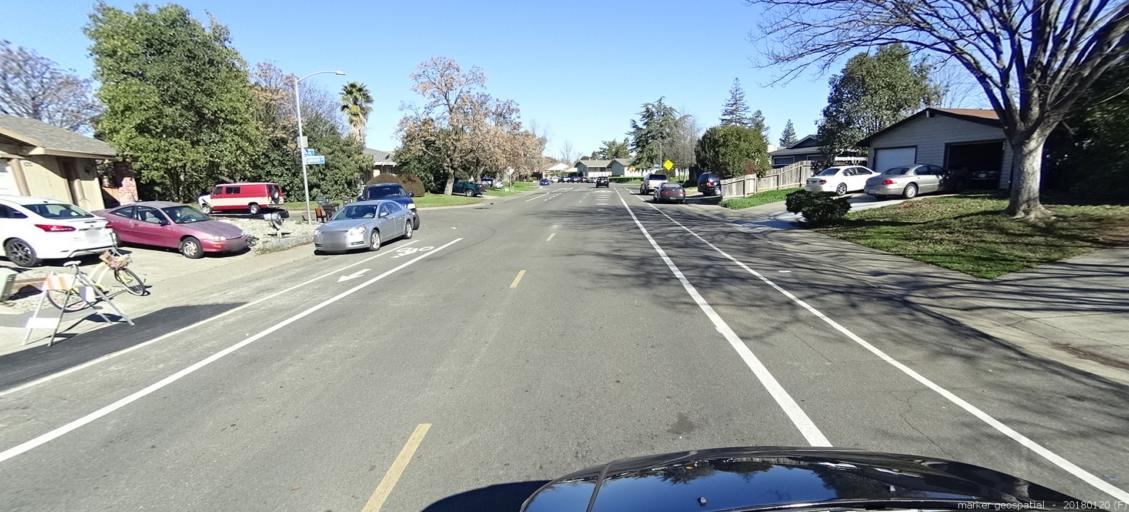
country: US
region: California
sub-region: Sacramento County
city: La Riviera
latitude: 38.5628
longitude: -121.3308
